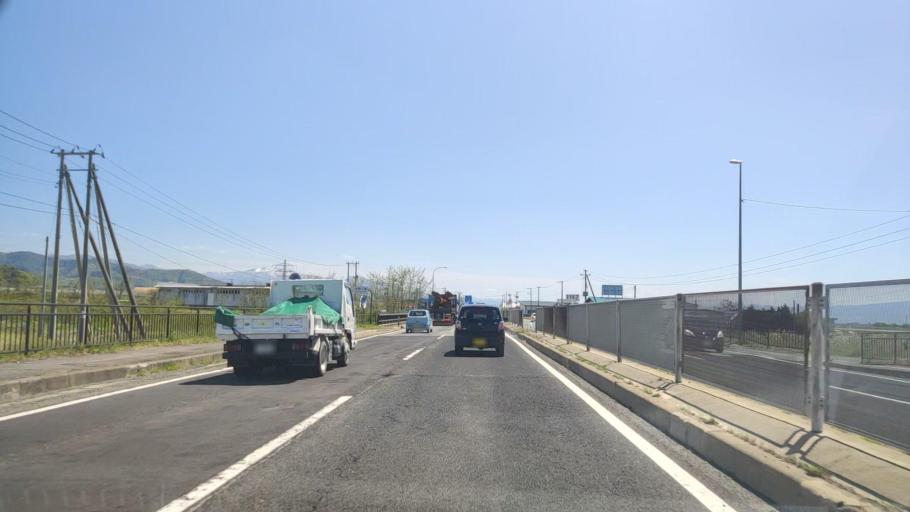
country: JP
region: Yamagata
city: Higashine
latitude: 38.4232
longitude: 140.3760
